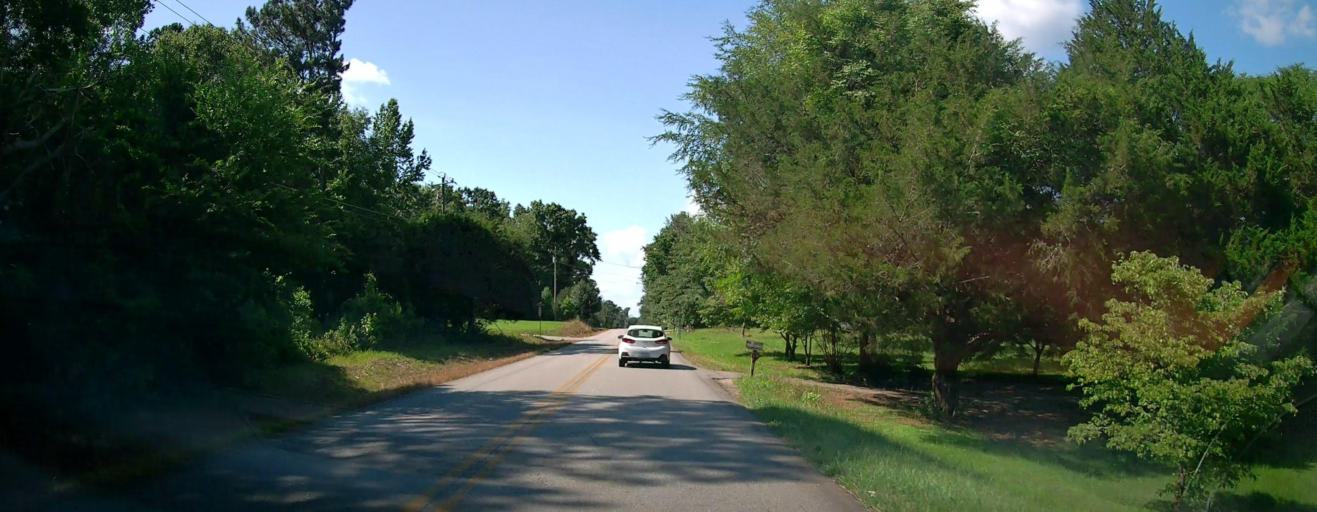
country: US
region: Georgia
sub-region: Spalding County
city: East Griffin
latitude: 33.2742
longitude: -84.1900
